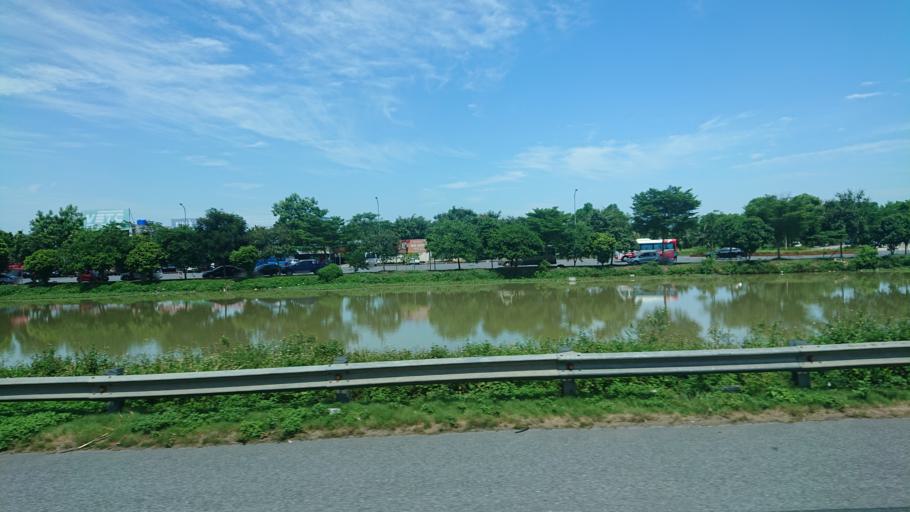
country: VN
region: Ha Nam
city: Thanh Pho Phu Ly
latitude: 20.5728
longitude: 105.9513
